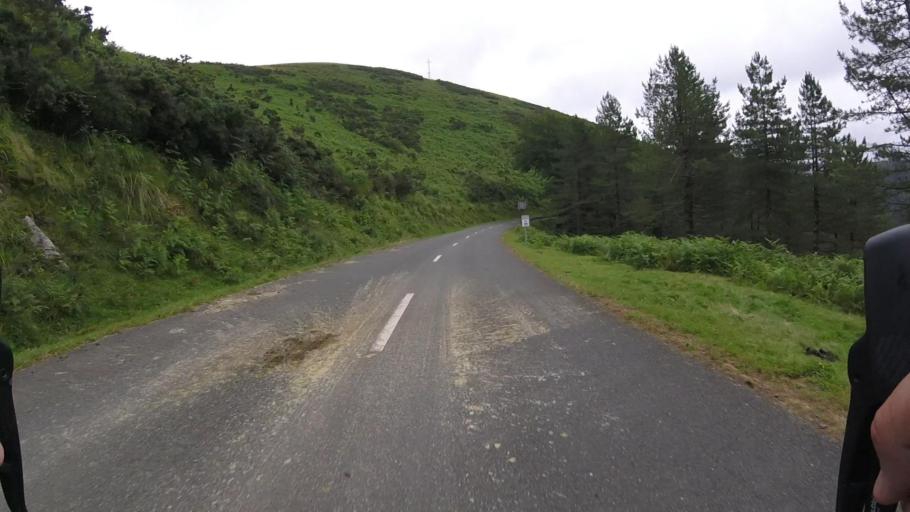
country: ES
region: Navarre
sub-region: Provincia de Navarra
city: Goizueta
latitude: 43.2447
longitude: -1.8109
